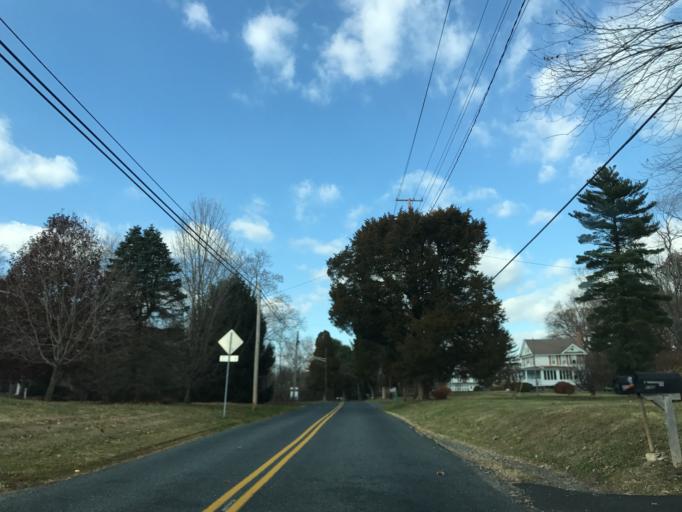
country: US
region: Maryland
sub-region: Harford County
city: Fallston
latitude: 39.5158
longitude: -76.4121
